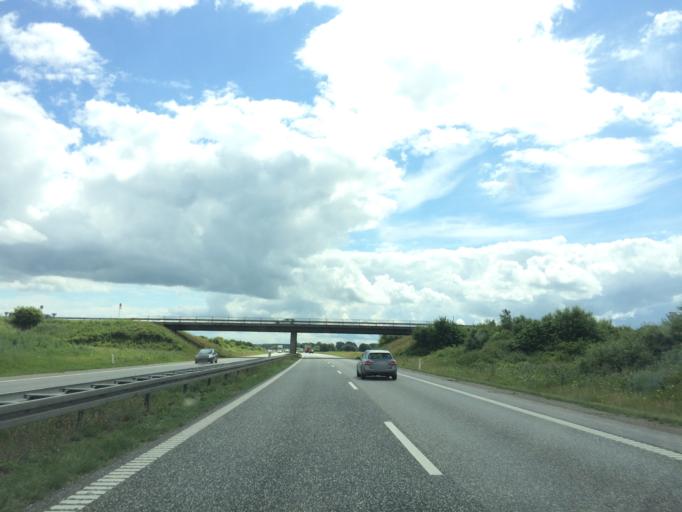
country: DK
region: North Denmark
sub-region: Mariagerfjord Kommune
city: Hobro
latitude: 56.6686
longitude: 9.7334
